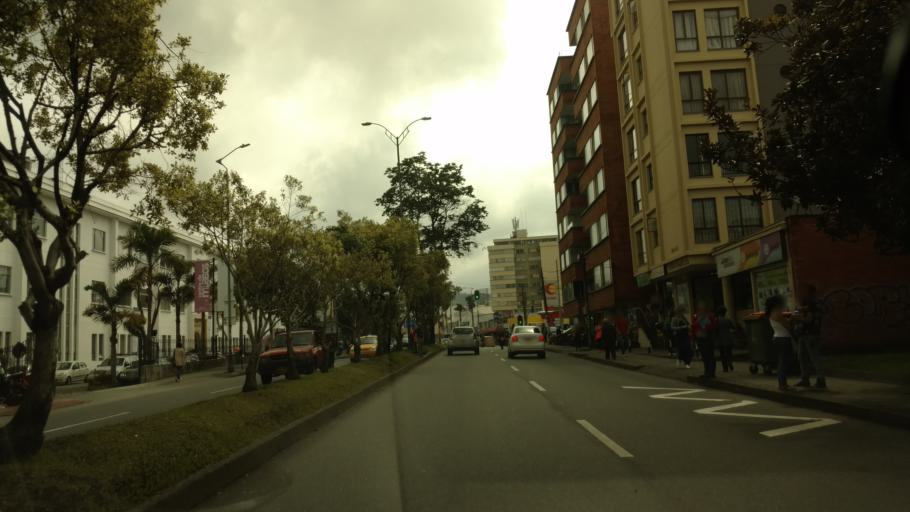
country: CO
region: Caldas
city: Manizales
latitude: 5.0612
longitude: -75.4911
